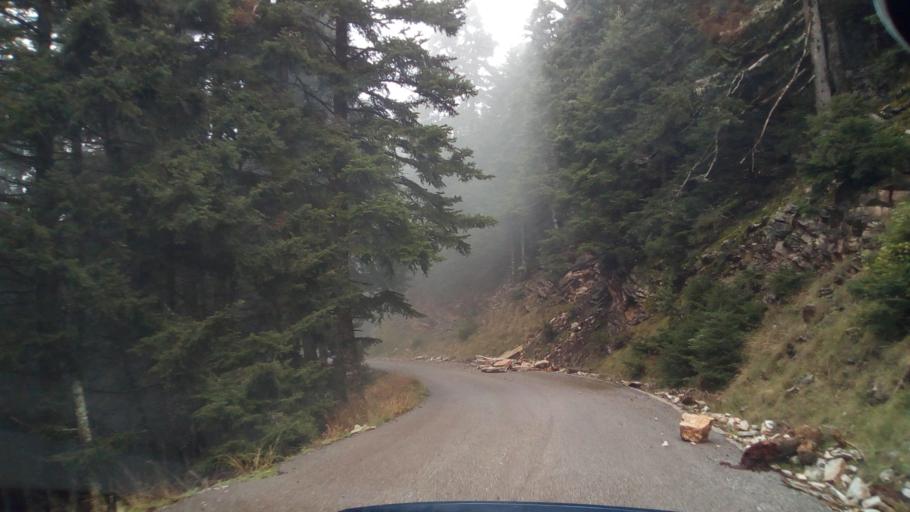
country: GR
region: West Greece
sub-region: Nomos Aitolias kai Akarnanias
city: Nafpaktos
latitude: 38.5384
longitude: 21.8555
